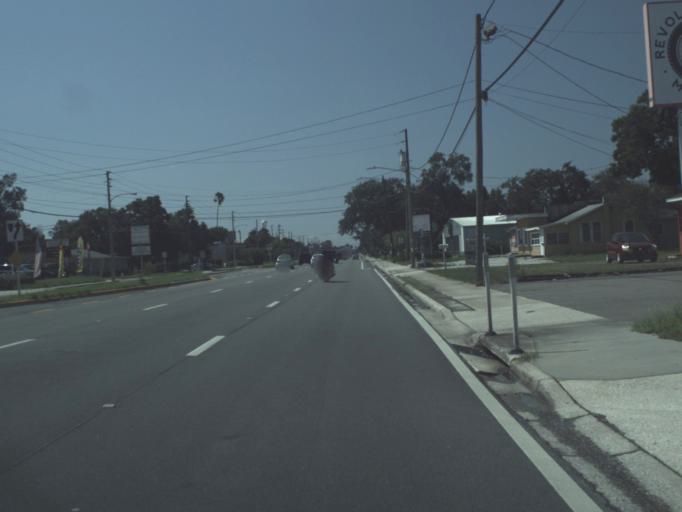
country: US
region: Florida
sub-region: Pinellas County
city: Pinellas Park
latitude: 27.8521
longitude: -82.7289
